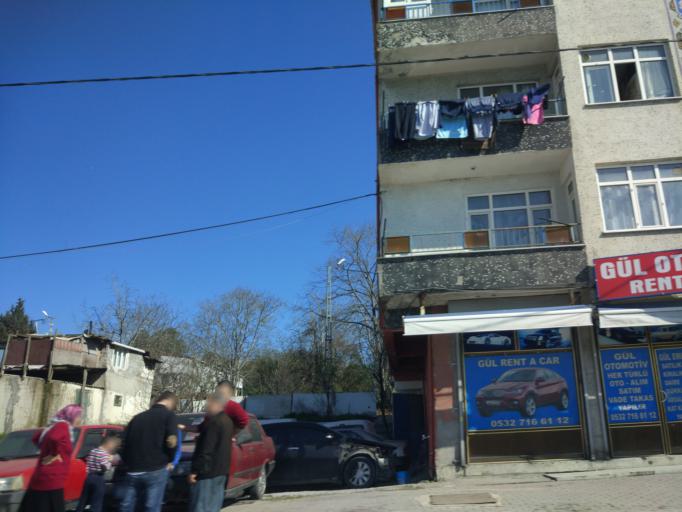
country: TR
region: Istanbul
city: Basaksehir
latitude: 41.0539
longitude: 28.7501
